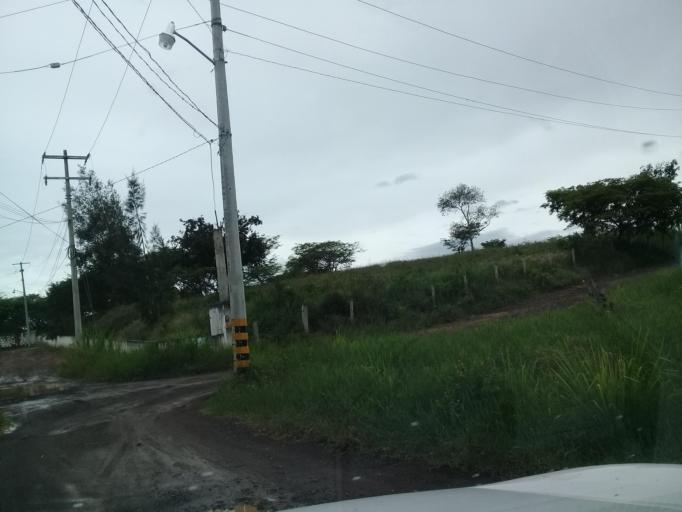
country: MX
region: Veracruz
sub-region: Emiliano Zapata
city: Jacarandas
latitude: 19.4977
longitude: -96.8437
